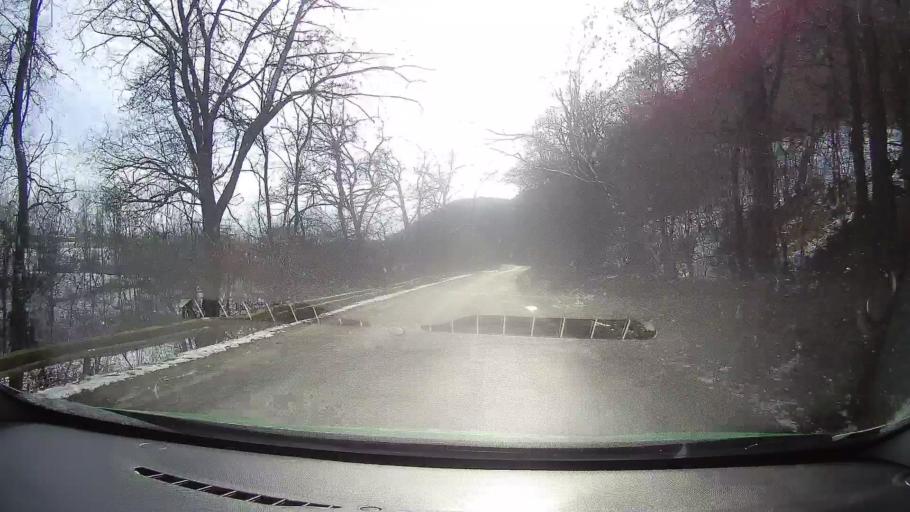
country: RO
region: Mures
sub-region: Municipiul Sighisoara
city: Sighisoara
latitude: 46.2001
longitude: 24.7690
